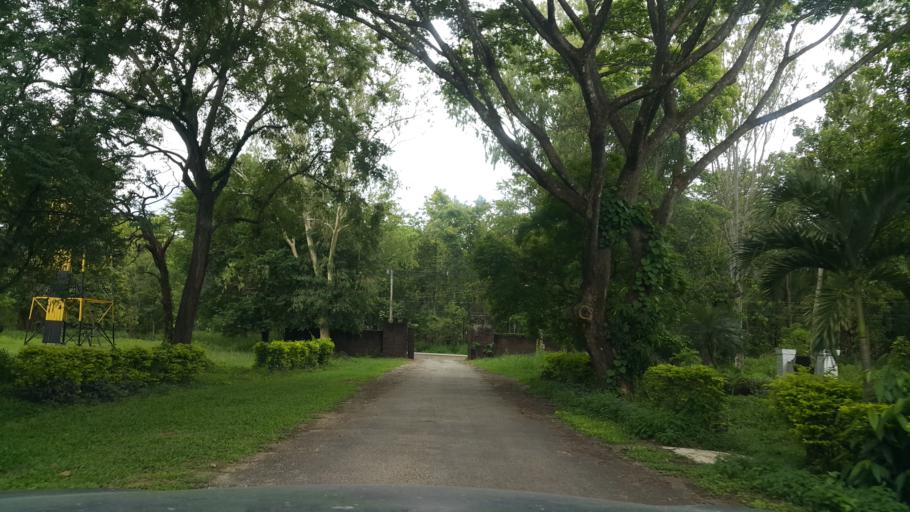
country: TH
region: Chiang Mai
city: Mae Taeng
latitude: 19.1834
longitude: 98.9670
